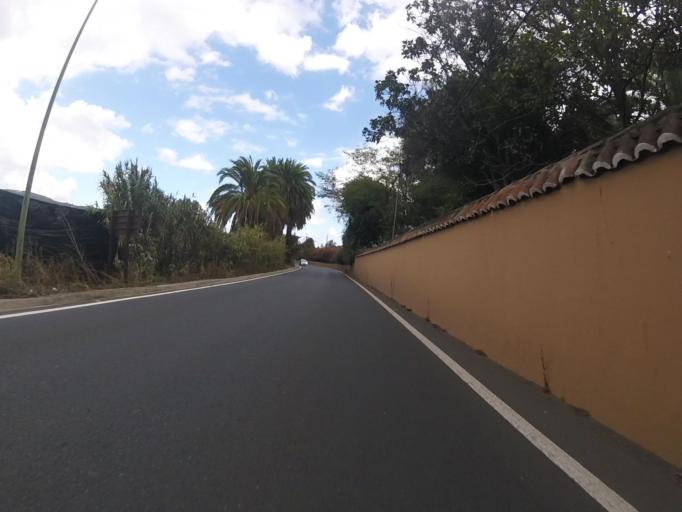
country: ES
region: Canary Islands
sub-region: Provincia de Las Palmas
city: Santa Brigida
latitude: 28.0263
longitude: -15.5026
